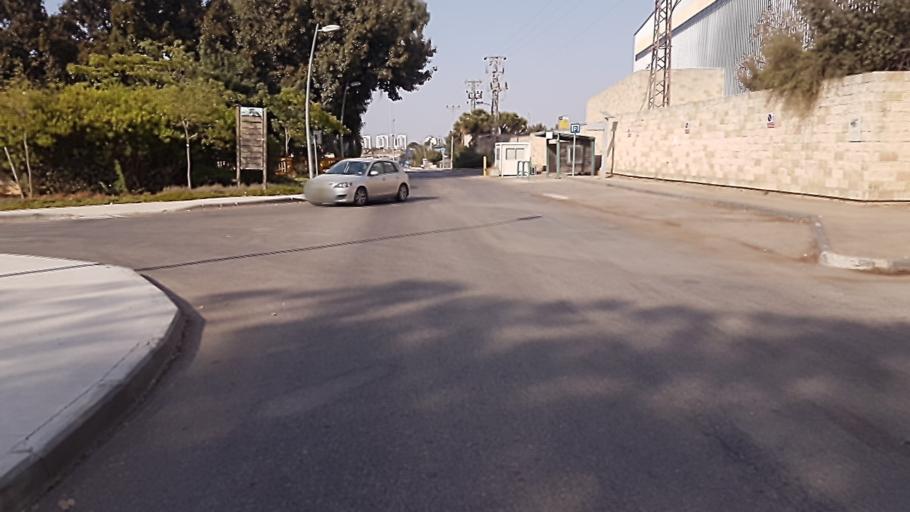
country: IL
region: Central District
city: Rosh Ha'Ayin
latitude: 32.0840
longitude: 34.9412
